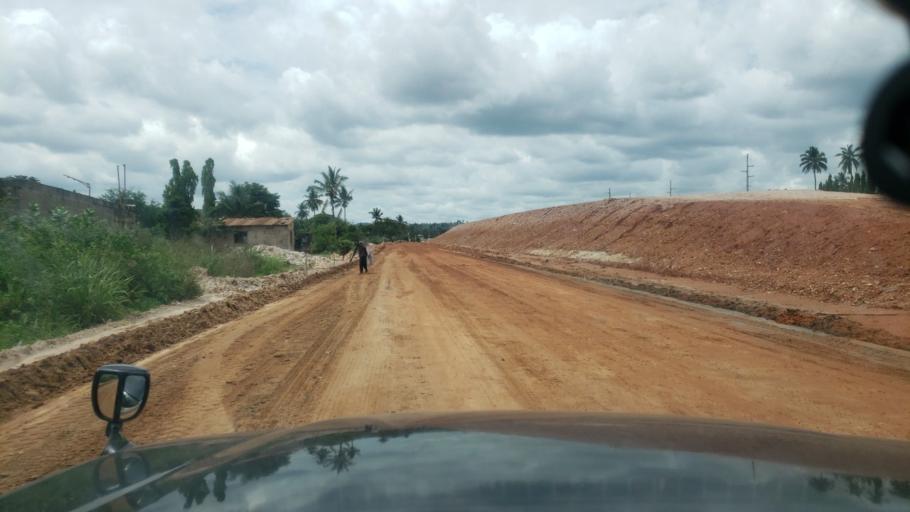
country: TZ
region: Pwani
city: Kisarawe
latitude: -6.8841
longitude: 39.1508
